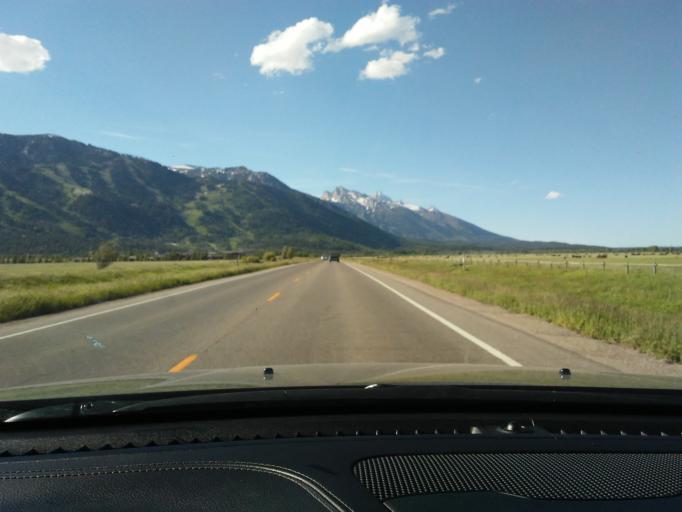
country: US
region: Wyoming
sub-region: Teton County
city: Moose Wilson Road
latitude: 43.5655
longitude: -110.8220
